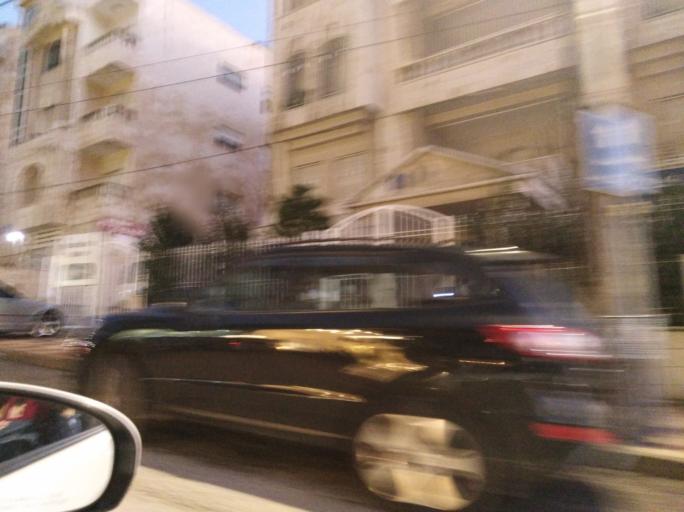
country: JO
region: Amman
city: Wadi as Sir
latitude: 31.9554
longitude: 35.8613
